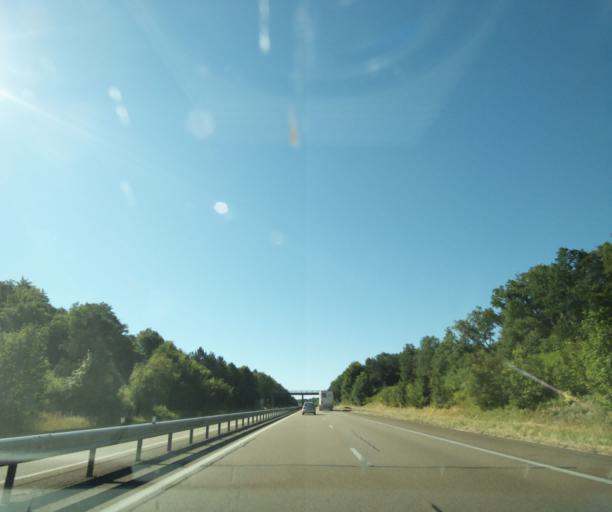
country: FR
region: Champagne-Ardenne
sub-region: Departement de la Haute-Marne
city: Chamarandes-Choignes
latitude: 48.0204
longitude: 5.0948
